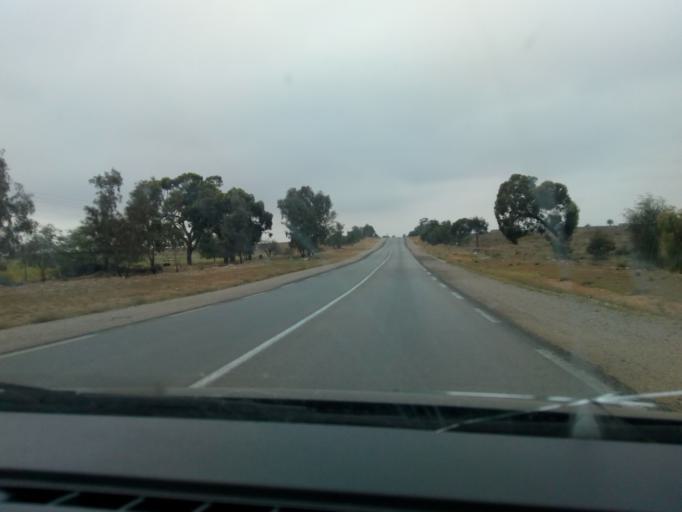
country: TN
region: Madanin
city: Medenine
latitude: 33.2693
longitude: 10.4672
